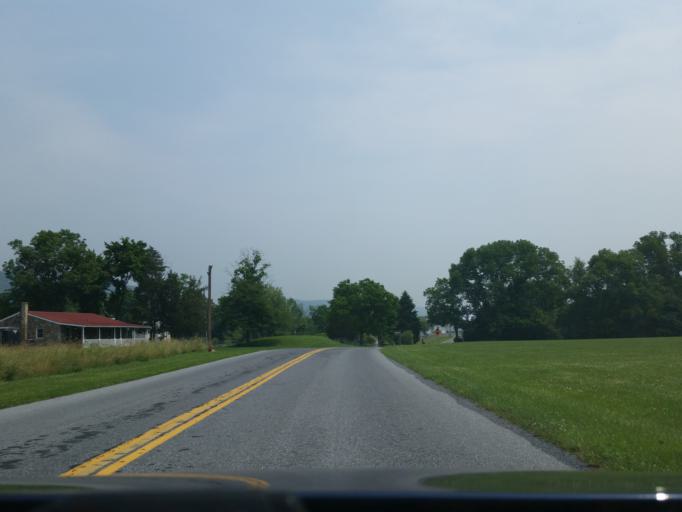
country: US
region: Pennsylvania
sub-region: Lebanon County
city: Palmyra
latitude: 40.4158
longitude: -76.6192
